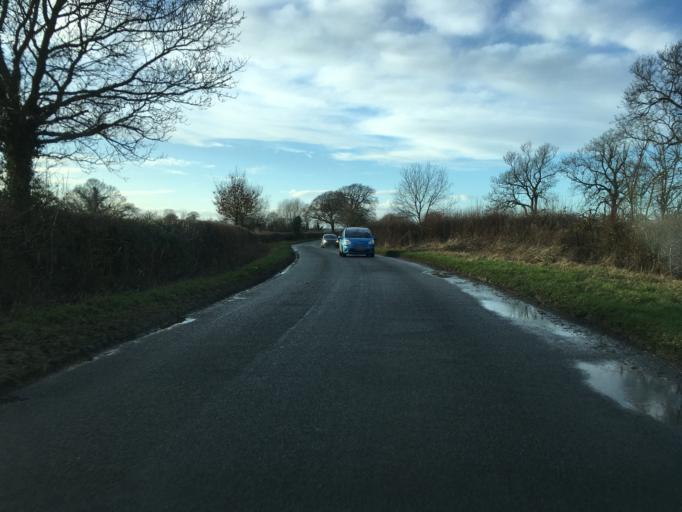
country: GB
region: England
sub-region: Warwickshire
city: Alcester
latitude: 52.2236
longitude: -1.8036
